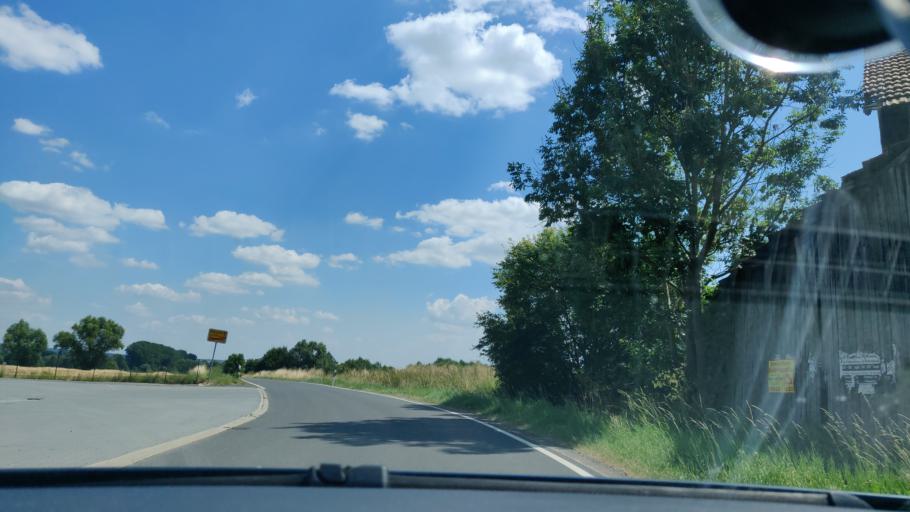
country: DE
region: Hesse
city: Gudensberg
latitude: 51.1560
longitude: 9.3566
